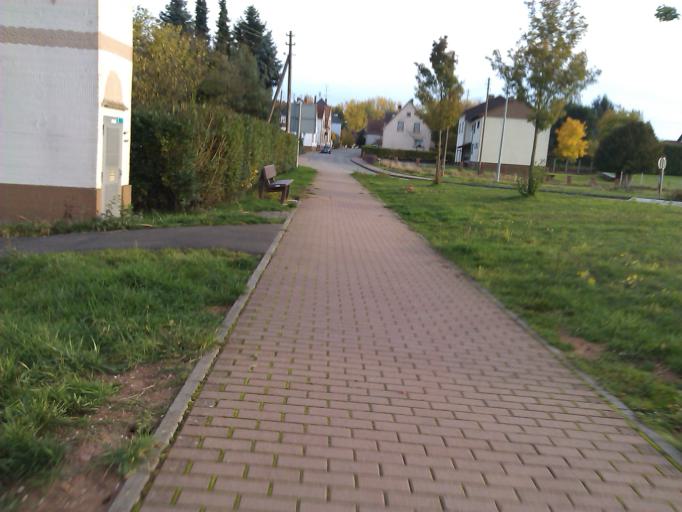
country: DE
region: Rheinland-Pfalz
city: Schneckenhausen
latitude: 49.5413
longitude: 7.7394
